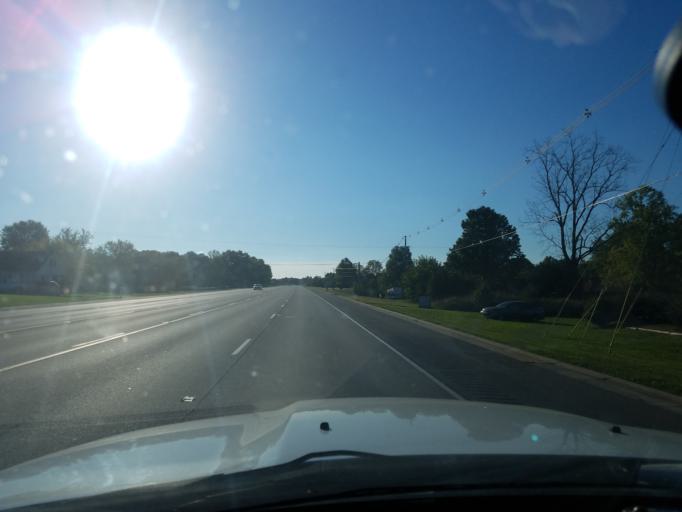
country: US
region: Kentucky
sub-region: Nelson County
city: Bardstown
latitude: 37.8563
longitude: -85.5142
